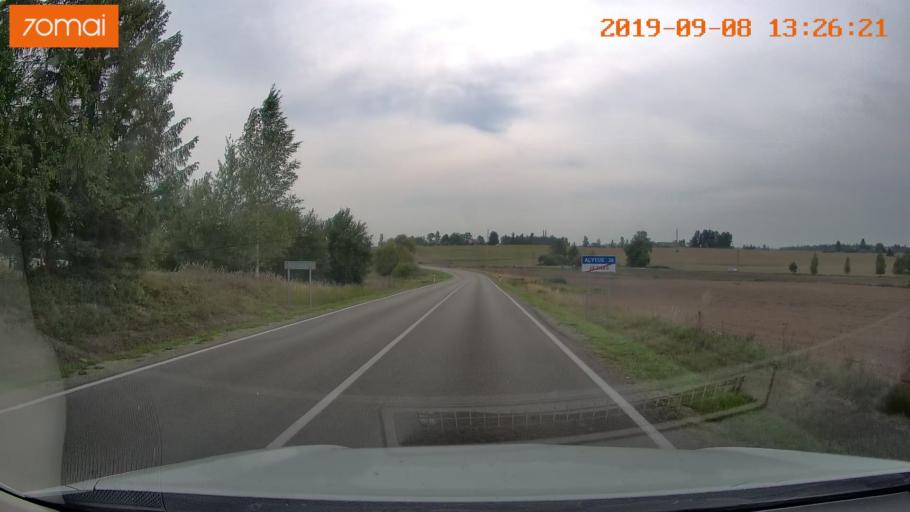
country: LT
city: Jieznas
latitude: 54.6003
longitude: 24.1622
